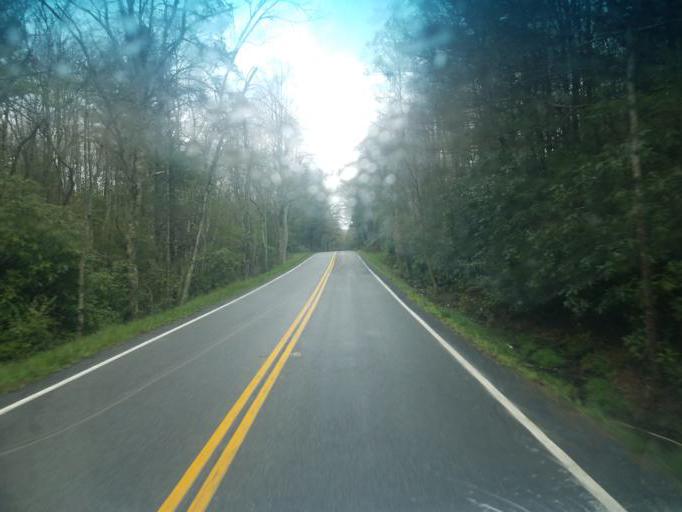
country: US
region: Virginia
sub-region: Smyth County
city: Chilhowie
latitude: 36.6531
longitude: -81.6984
